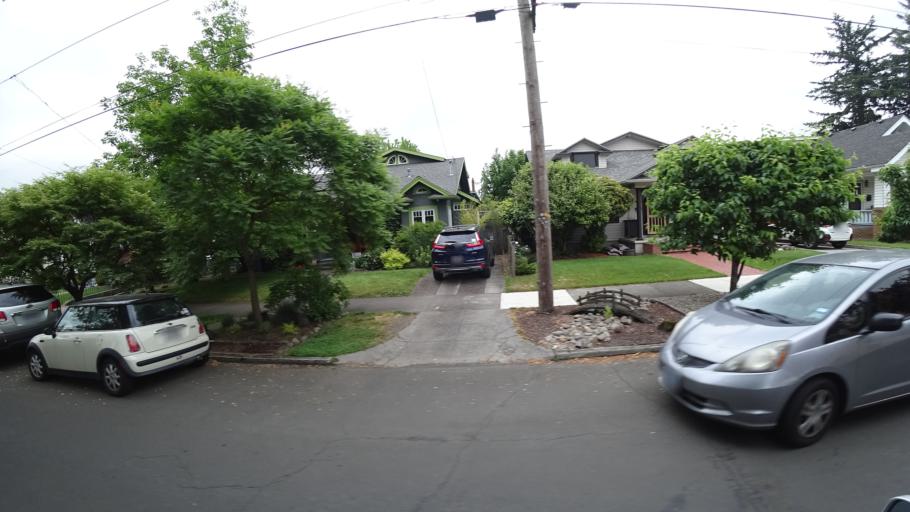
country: US
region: Oregon
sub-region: Multnomah County
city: Portland
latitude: 45.5431
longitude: -122.6077
